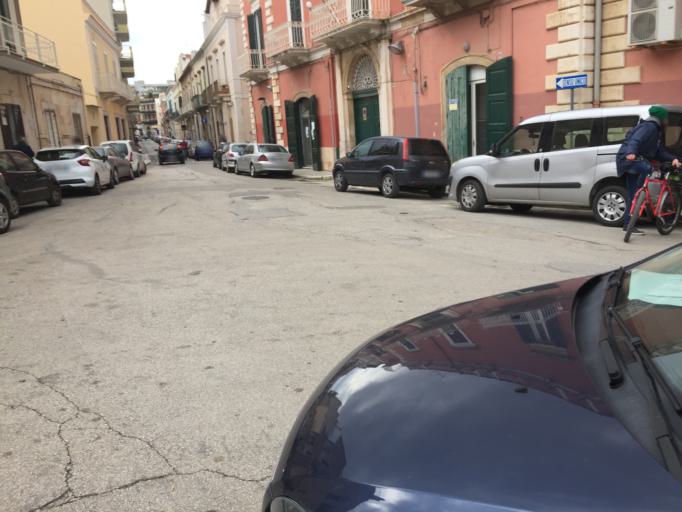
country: IT
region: Apulia
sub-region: Provincia di Bari
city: Bitonto
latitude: 41.1111
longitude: 16.6932
